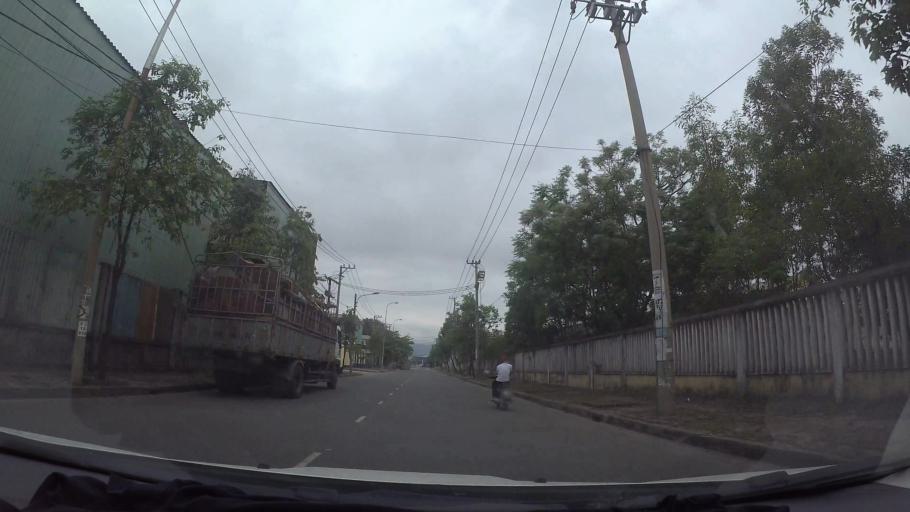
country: VN
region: Da Nang
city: Lien Chieu
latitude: 16.0847
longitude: 108.1393
